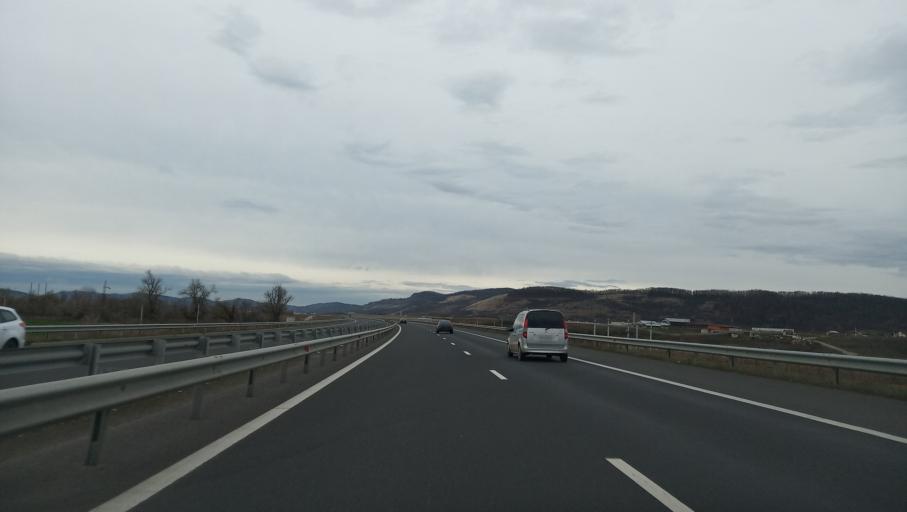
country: RO
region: Hunedoara
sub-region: Comuna Soimus
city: Soimus
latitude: 45.9061
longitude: 22.9227
